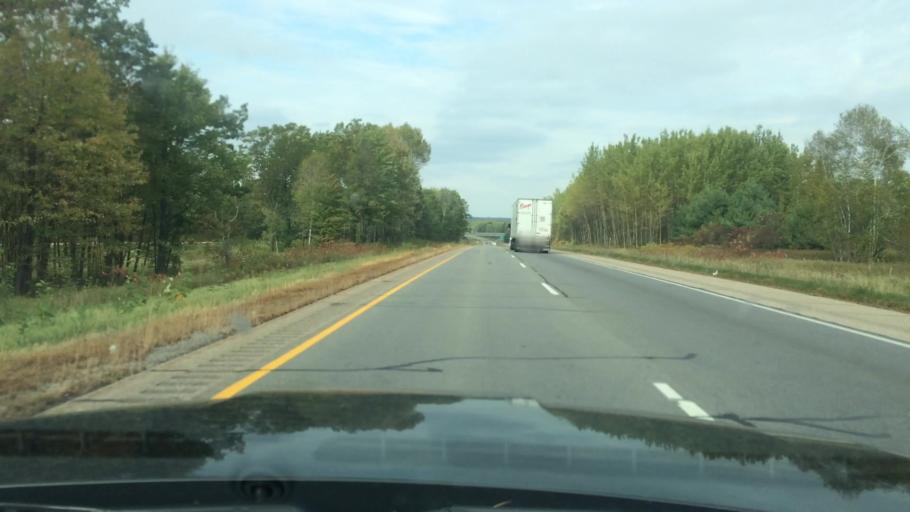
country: US
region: Wisconsin
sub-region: Marathon County
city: Mosinee
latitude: 44.7060
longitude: -89.6542
